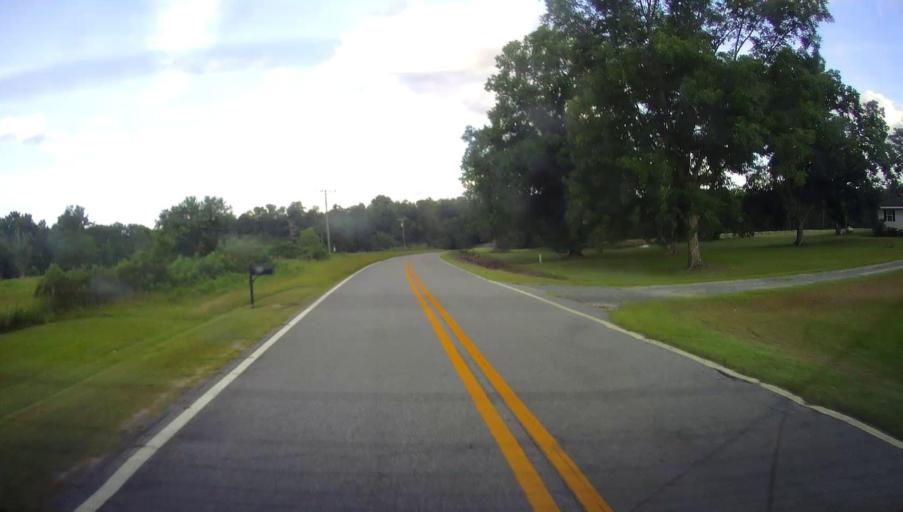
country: US
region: Georgia
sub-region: Crawford County
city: Knoxville
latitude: 32.7550
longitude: -83.9174
